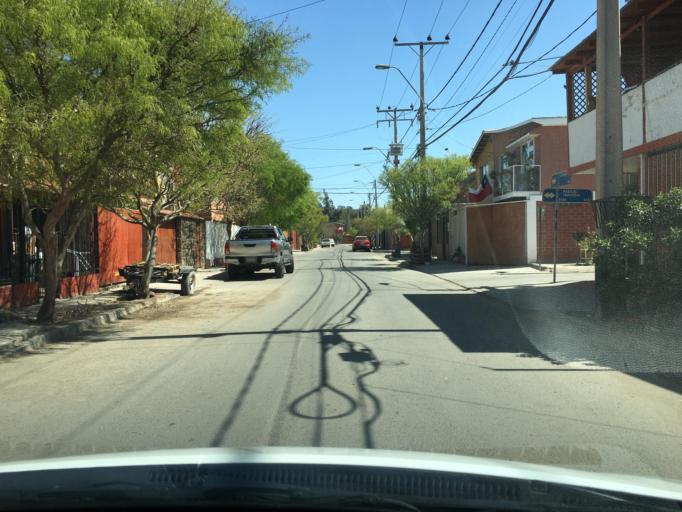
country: CL
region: Atacama
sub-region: Provincia de Copiapo
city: Copiapo
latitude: -27.4094
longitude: -70.2825
